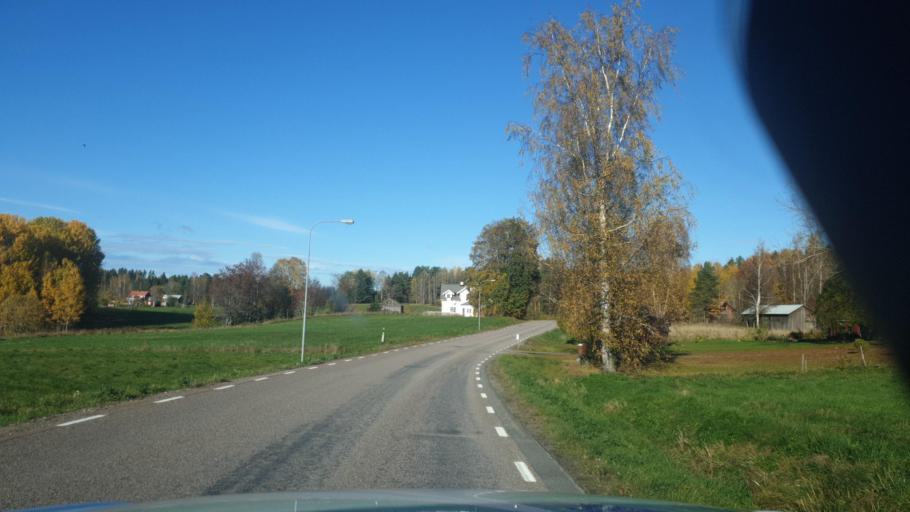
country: SE
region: Vaermland
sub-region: Arvika Kommun
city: Arvika
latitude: 59.6024
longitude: 12.7595
